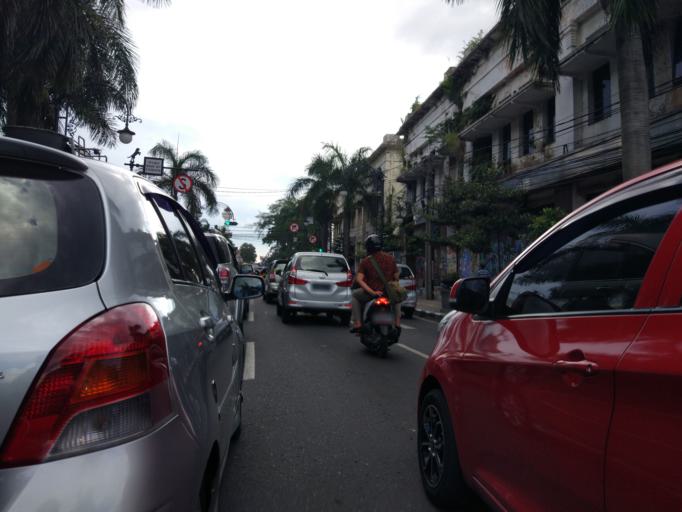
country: ID
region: West Java
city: Bandung
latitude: -6.9218
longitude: 107.6128
